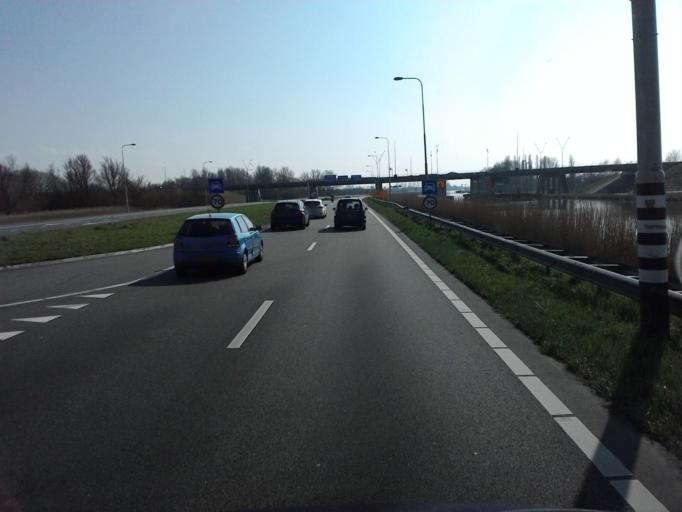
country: NL
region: North Holland
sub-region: Gemeente Zaanstad
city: Zaanstad
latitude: 52.4765
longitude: 4.7701
